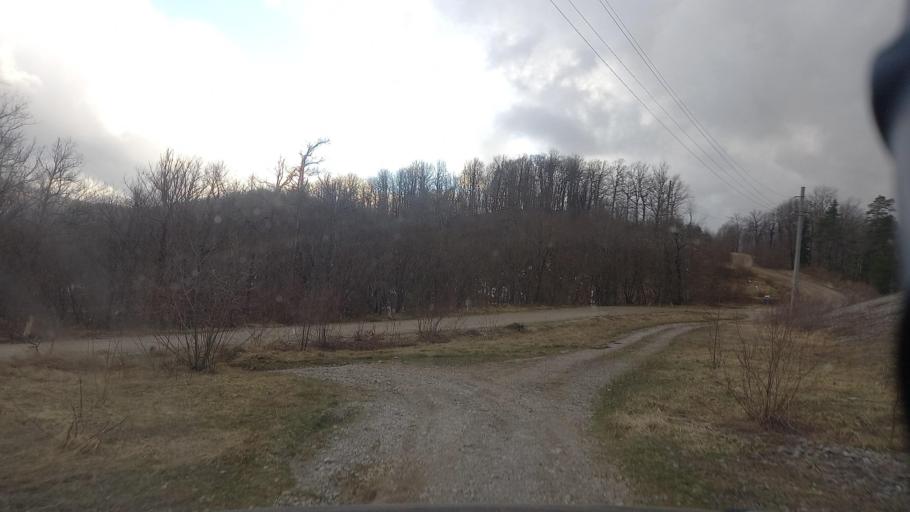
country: RU
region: Krasnodarskiy
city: Dzhubga
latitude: 44.5244
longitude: 38.7729
